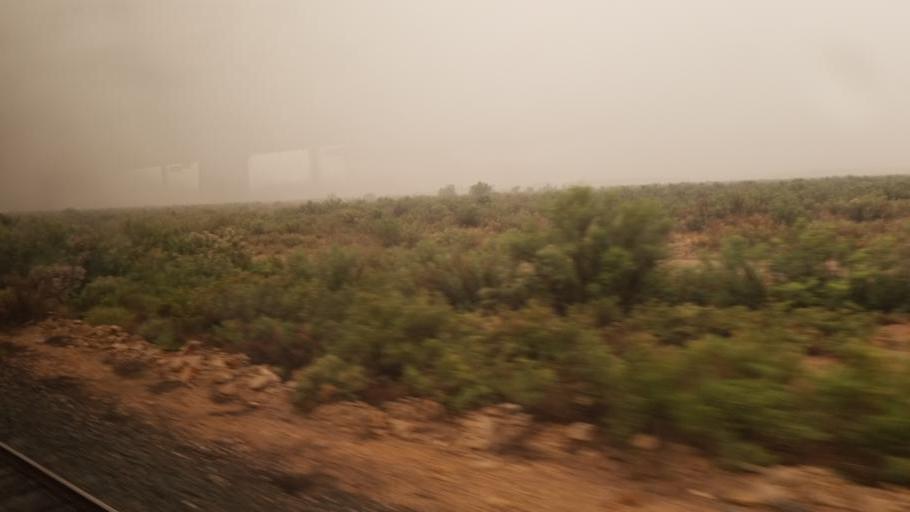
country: US
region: Arizona
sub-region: Navajo County
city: Joseph City
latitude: 34.9526
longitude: -110.3488
